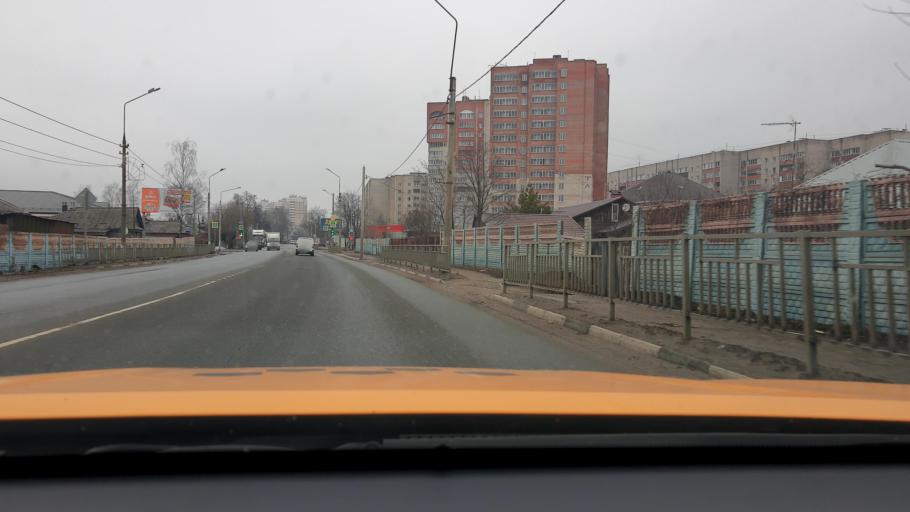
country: RU
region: Moskovskaya
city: Noginsk
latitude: 55.8724
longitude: 38.4353
